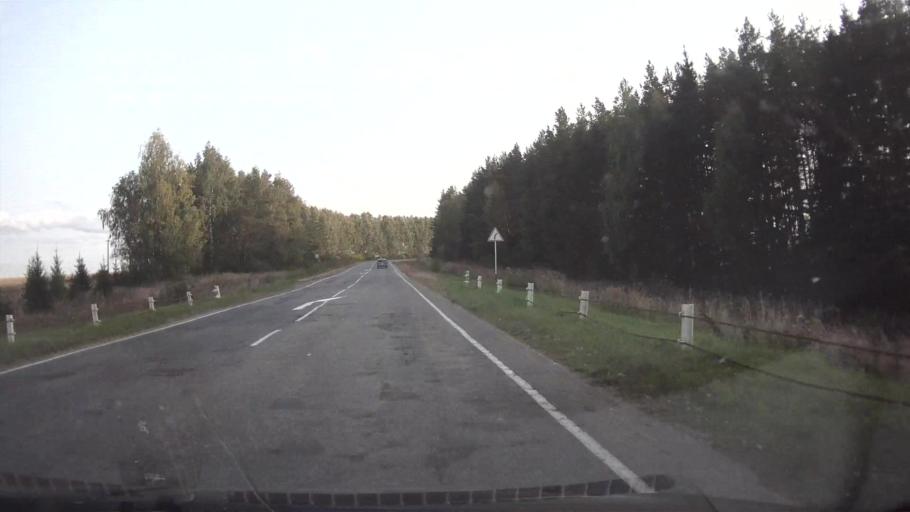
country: RU
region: Mariy-El
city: Kuzhener
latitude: 56.8618
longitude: 48.7563
